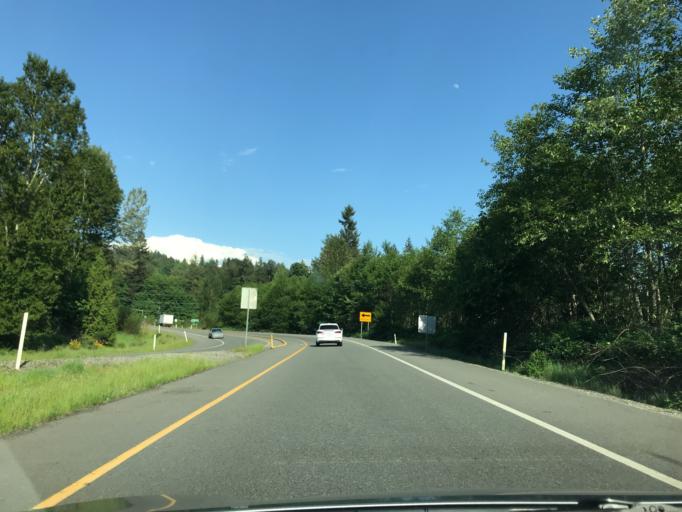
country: US
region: Washington
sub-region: King County
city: Hobart
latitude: 47.4335
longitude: -121.9771
